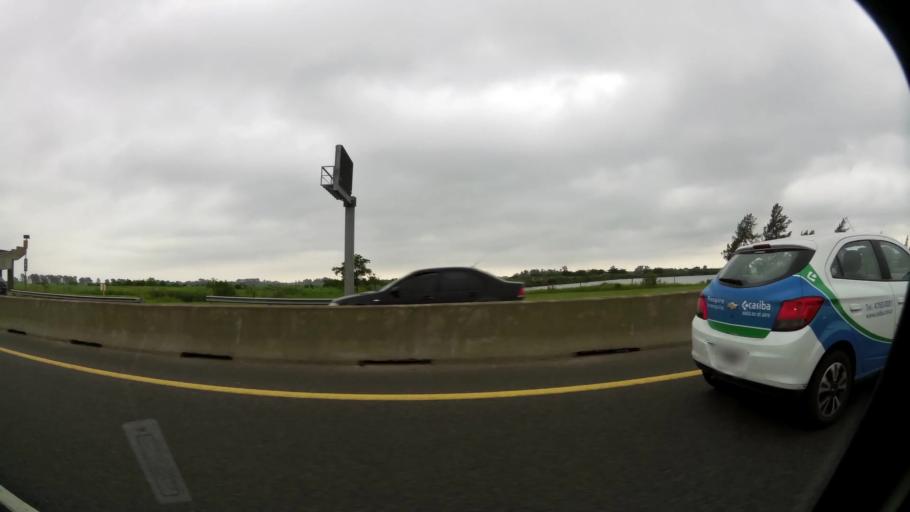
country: AR
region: Buenos Aires
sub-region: Partido de La Plata
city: La Plata
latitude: -34.8772
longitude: -57.9681
